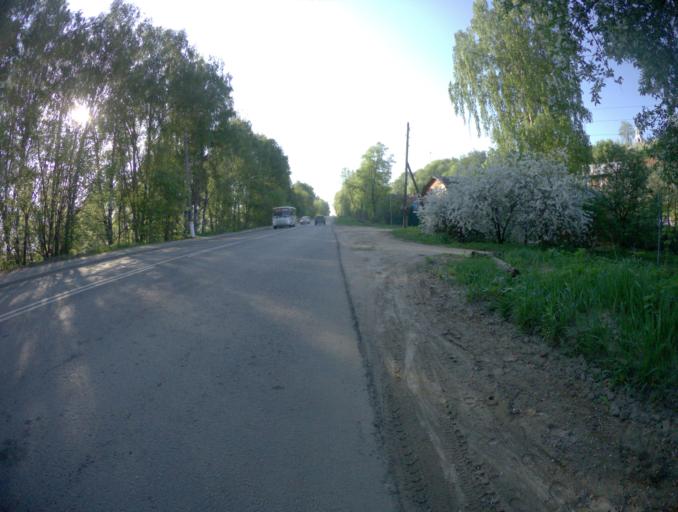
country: RU
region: Vladimir
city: Vyazniki
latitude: 56.2434
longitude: 42.1650
